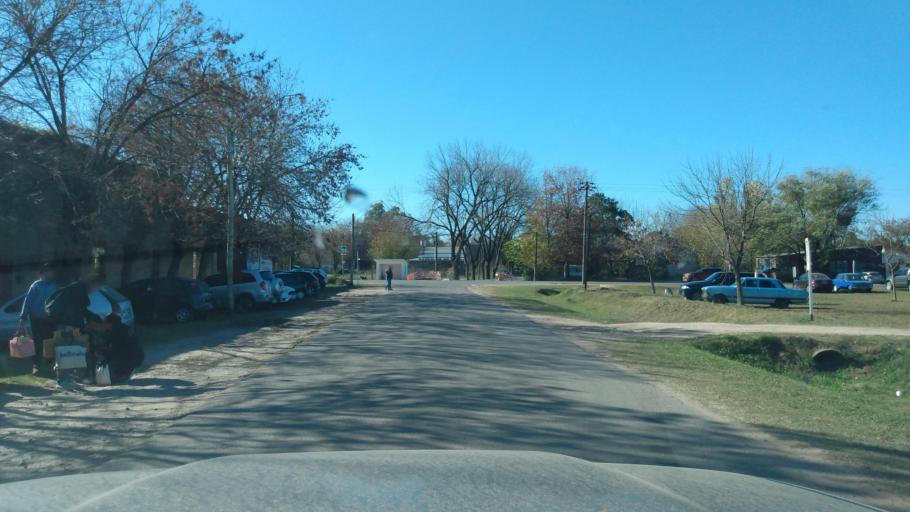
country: AR
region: Buenos Aires
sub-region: Partido de Lujan
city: Lujan
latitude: -34.4846
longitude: -59.2223
